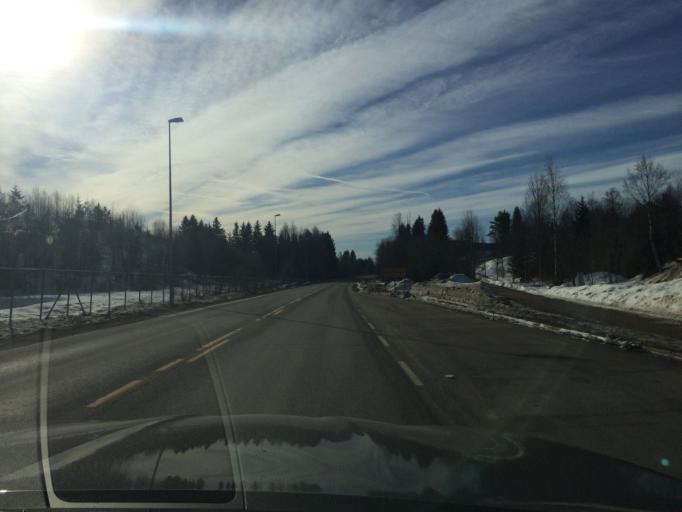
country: NO
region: Hedmark
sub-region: Trysil
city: Innbygda
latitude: 61.3144
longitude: 12.2549
